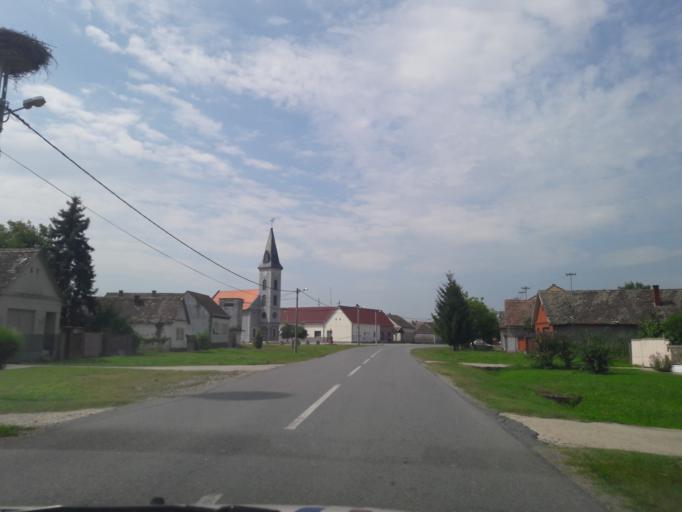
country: HR
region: Osjecko-Baranjska
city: Bizovac
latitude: 45.5111
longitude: 18.4700
